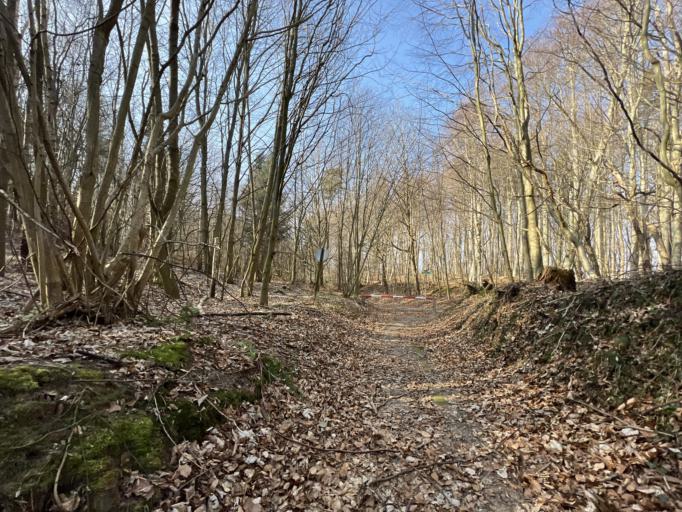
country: DE
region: Mecklenburg-Vorpommern
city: Sagard
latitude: 54.4807
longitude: 13.5546
